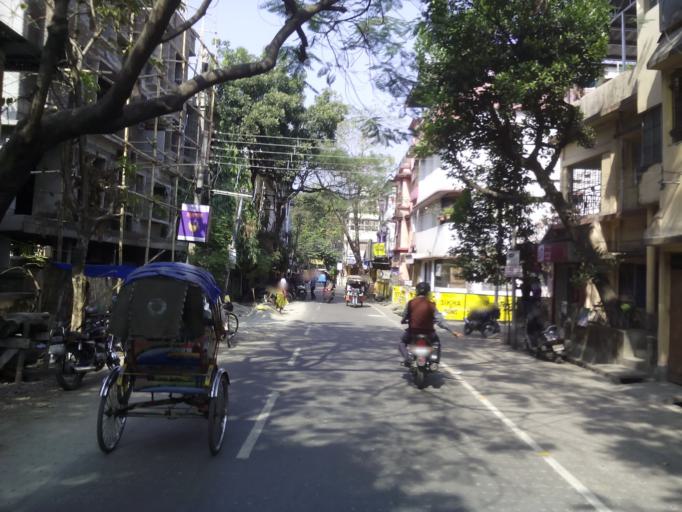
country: IN
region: West Bengal
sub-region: Darjiling
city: Shiliguri
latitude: 26.7089
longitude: 88.4340
